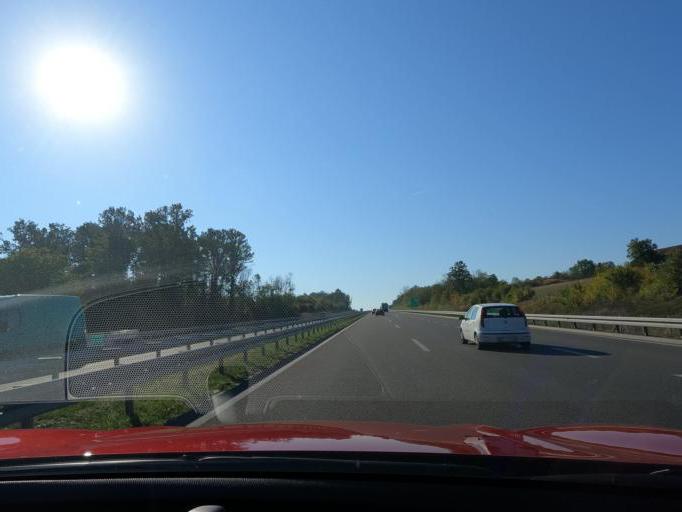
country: RS
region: Central Serbia
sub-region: Kolubarski Okrug
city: Ub
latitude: 44.4753
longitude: 20.1156
